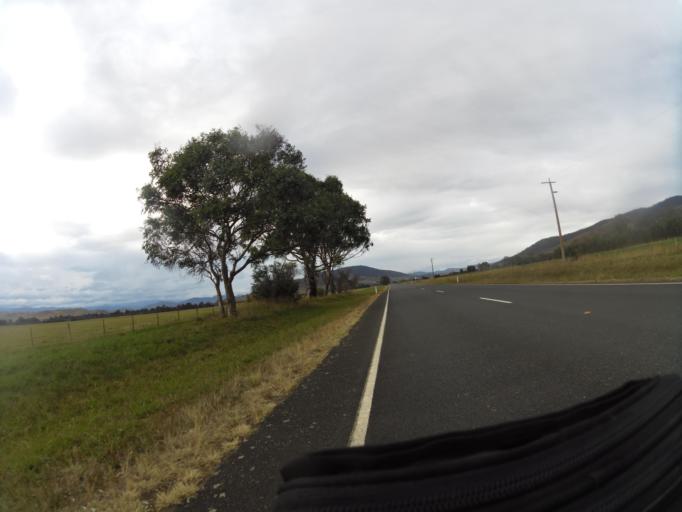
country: AU
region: New South Wales
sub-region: Snowy River
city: Jindabyne
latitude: -36.0964
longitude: 147.9818
